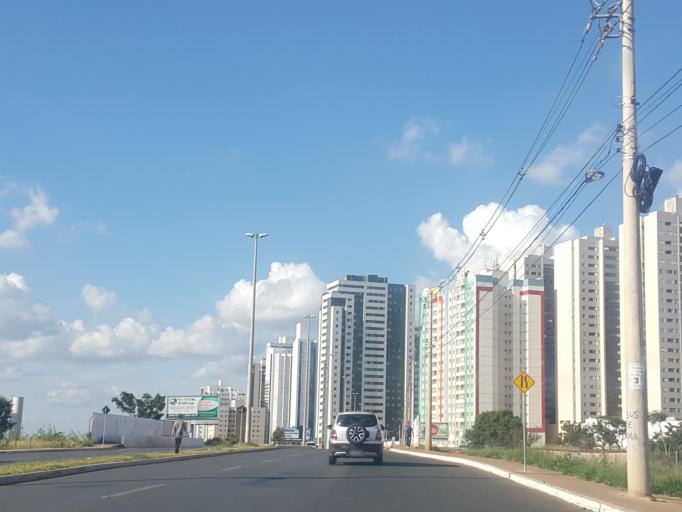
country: BR
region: Federal District
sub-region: Brasilia
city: Brasilia
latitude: -15.8374
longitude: -48.0440
